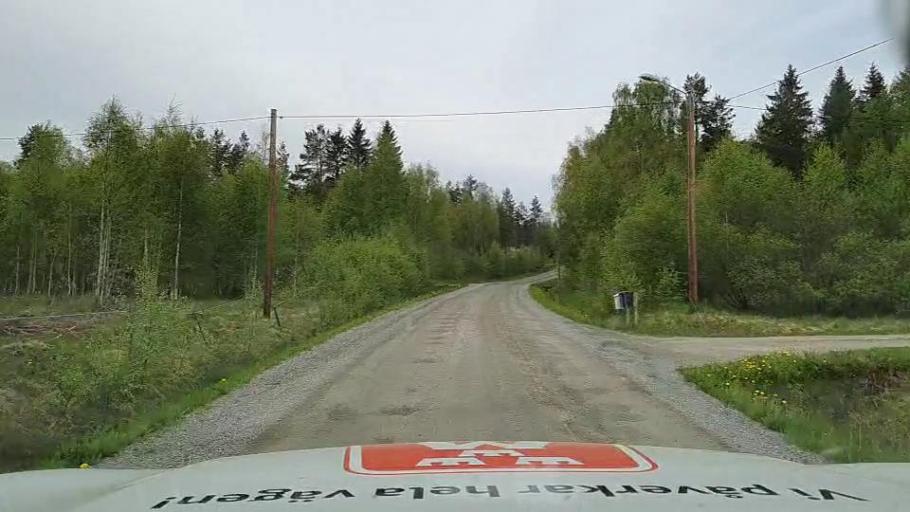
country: SE
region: Jaemtland
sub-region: Braecke Kommun
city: Braecke
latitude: 62.4550
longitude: 14.9151
